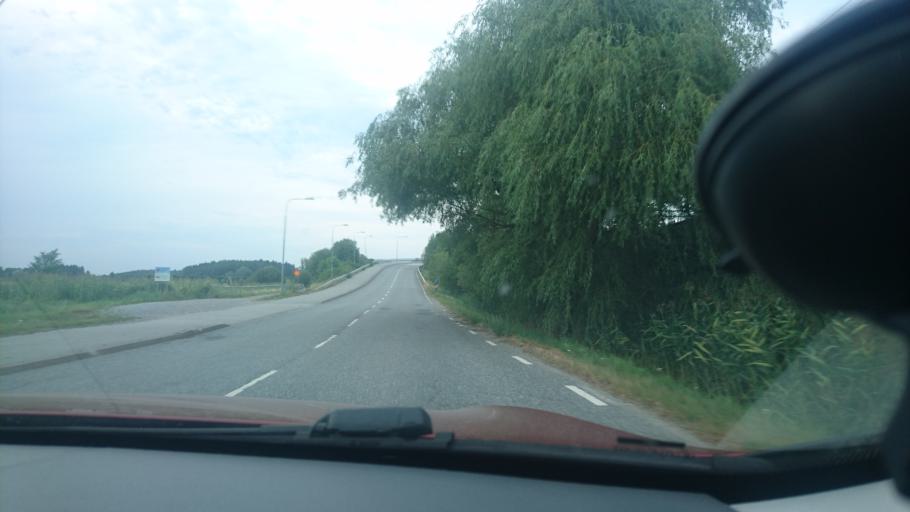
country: SE
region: Stockholm
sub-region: Upplands Vasby Kommun
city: Upplands Vaesby
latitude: 59.5262
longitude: 17.9010
